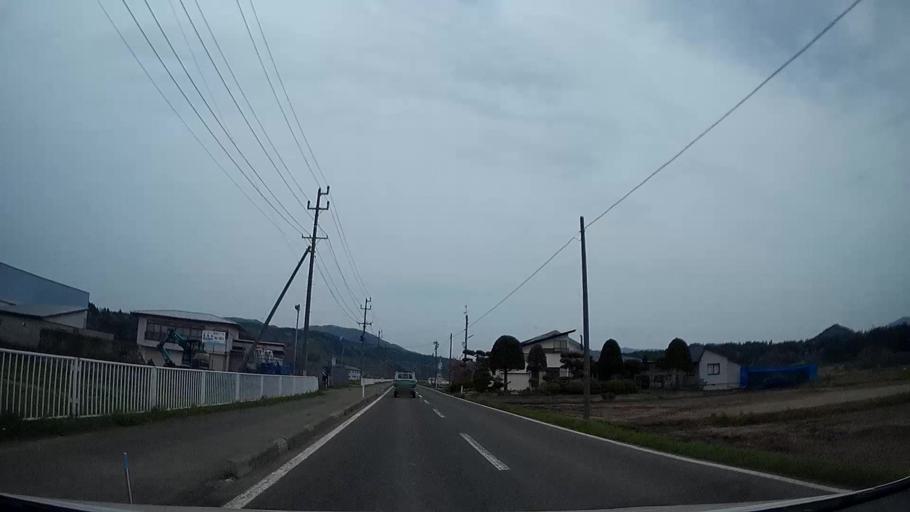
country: JP
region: Akita
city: Hanawa
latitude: 40.2809
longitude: 140.8008
